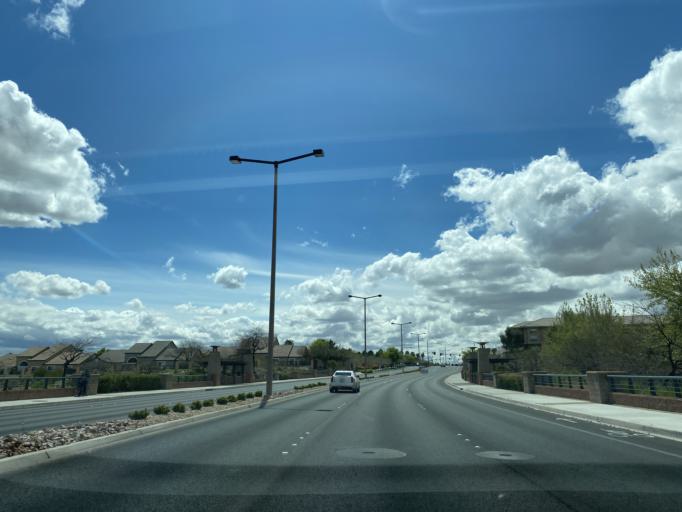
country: US
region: Nevada
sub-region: Clark County
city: Summerlin South
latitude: 36.1635
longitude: -115.3233
